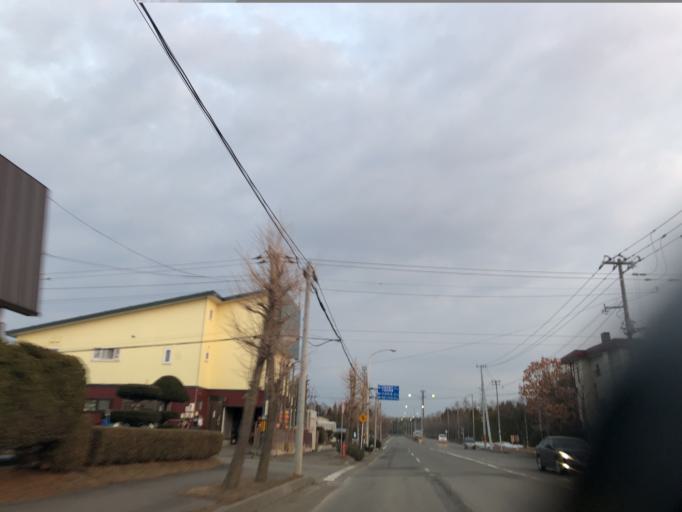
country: JP
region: Hokkaido
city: Chitose
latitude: 42.8253
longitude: 141.6698
